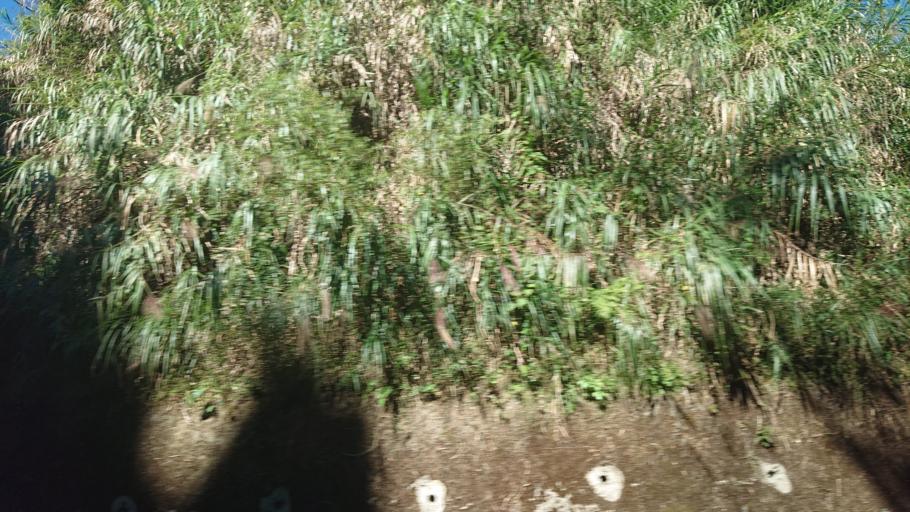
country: TW
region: Taiwan
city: Lugu
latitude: 23.4955
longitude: 120.7979
